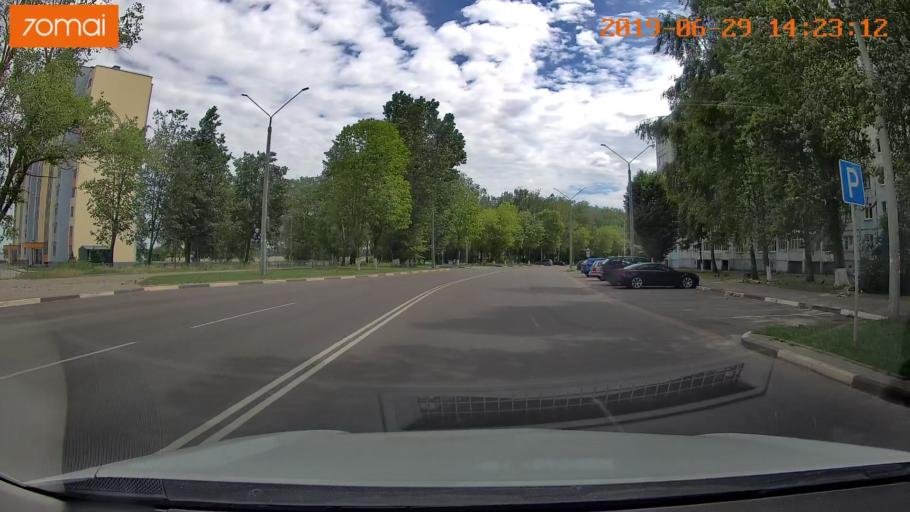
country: BY
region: Minsk
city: Salihorsk
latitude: 52.7873
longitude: 27.5539
